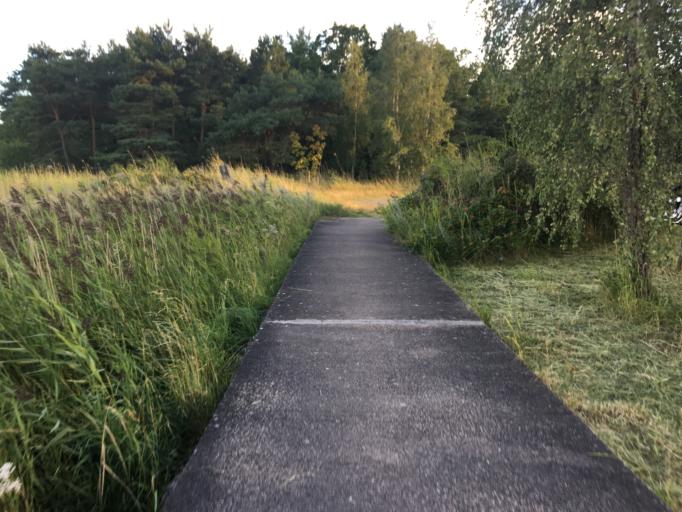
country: SE
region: Kalmar
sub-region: Kalmar Kommun
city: Kalmar
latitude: 56.6928
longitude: 16.3636
